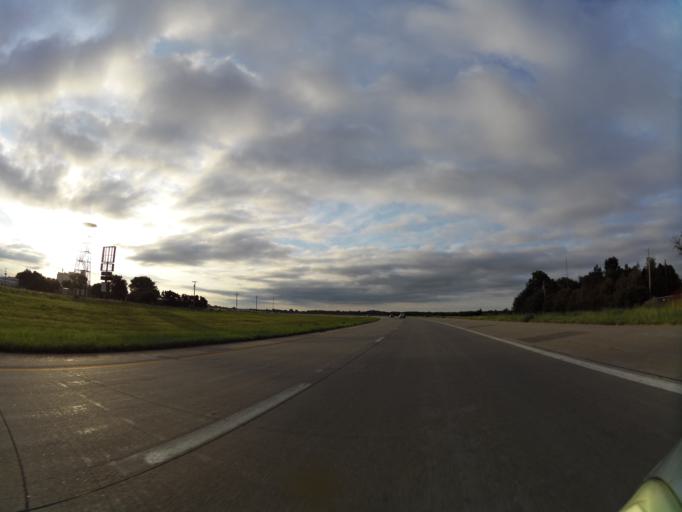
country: US
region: Kansas
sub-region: Reno County
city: Haven
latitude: 37.8980
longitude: -97.7918
